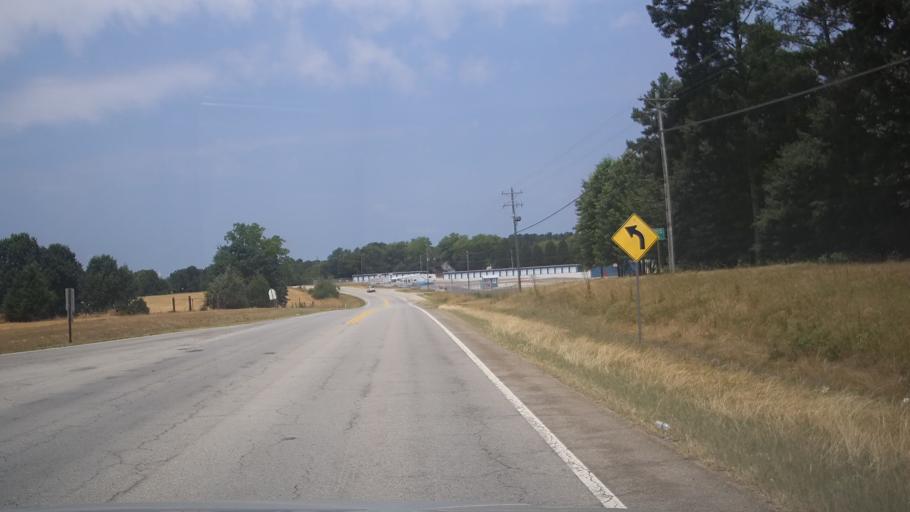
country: US
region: Georgia
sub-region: Hart County
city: Hartwell
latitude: 34.3401
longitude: -82.8469
